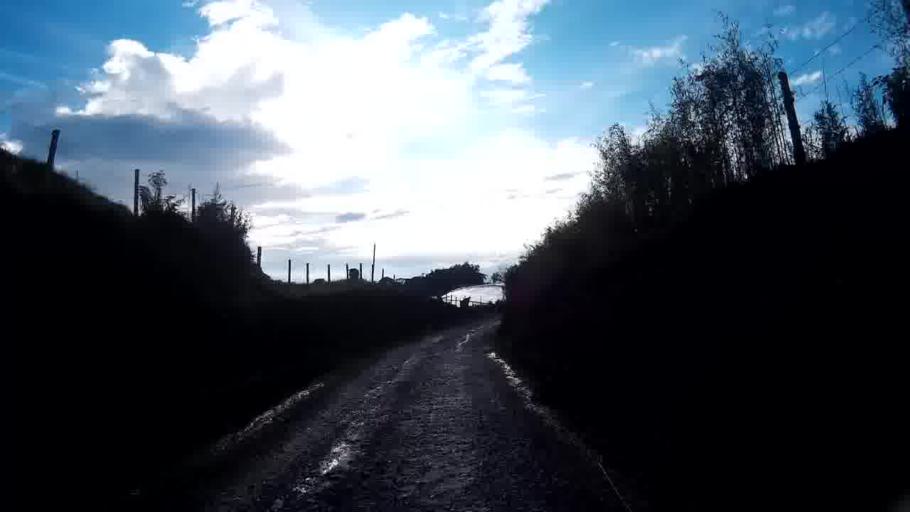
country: CO
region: Quindio
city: Filandia
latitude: 4.6976
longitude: -75.6717
